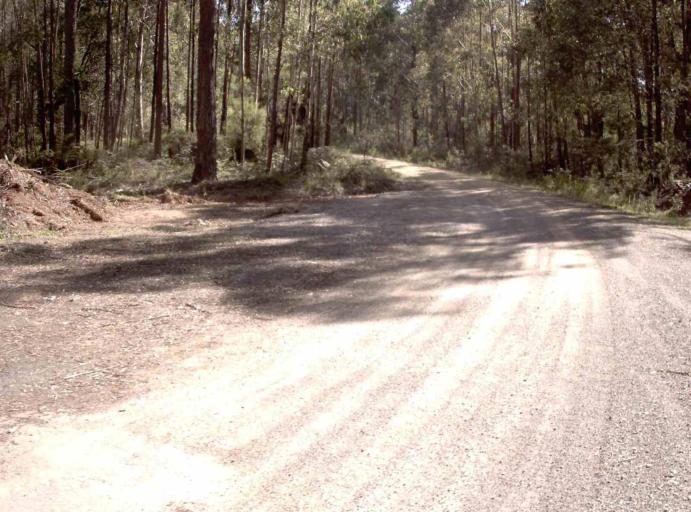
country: AU
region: New South Wales
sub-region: Bombala
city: Bombala
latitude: -37.3871
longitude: 148.6237
